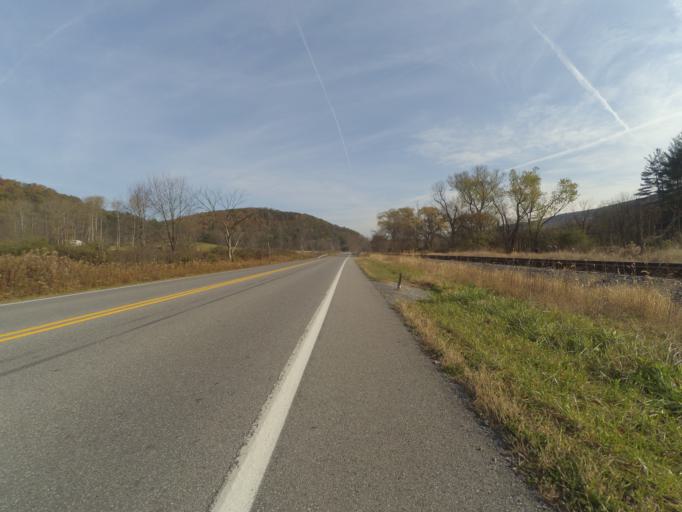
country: US
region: Pennsylvania
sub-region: Centre County
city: Park Forest Village
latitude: 40.8488
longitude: -77.9712
